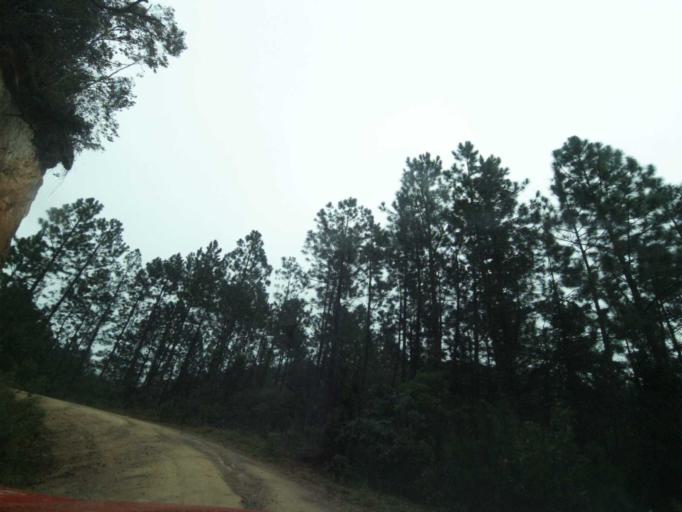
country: BR
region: Santa Catarina
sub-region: Anitapolis
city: Anitapolis
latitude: -27.9203
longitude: -49.1946
